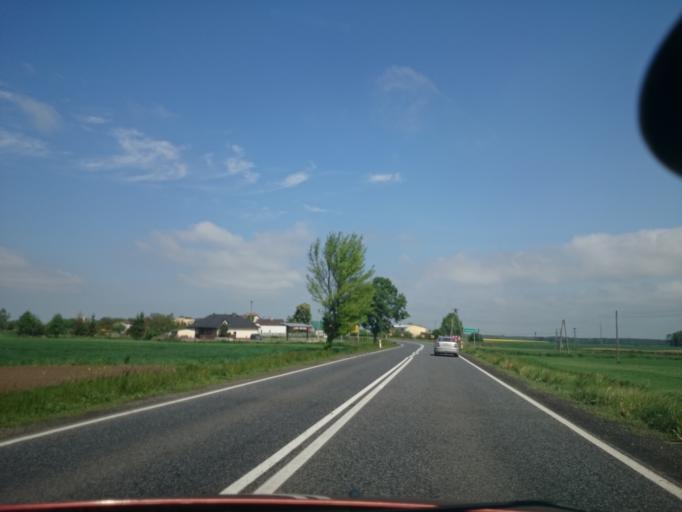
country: PL
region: Opole Voivodeship
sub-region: Powiat opolski
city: Dabrowa
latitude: 50.7182
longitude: 17.7706
